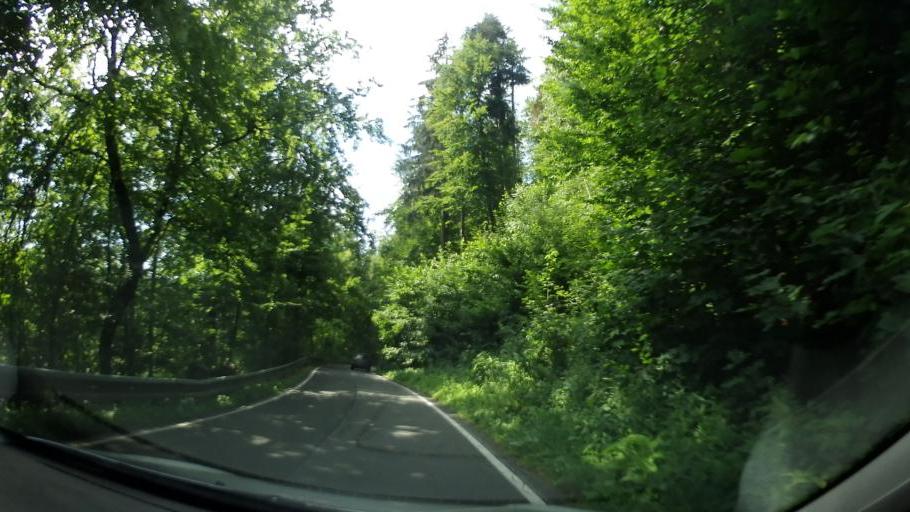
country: CZ
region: Olomoucky
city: Zabreh
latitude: 49.8651
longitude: 16.8283
